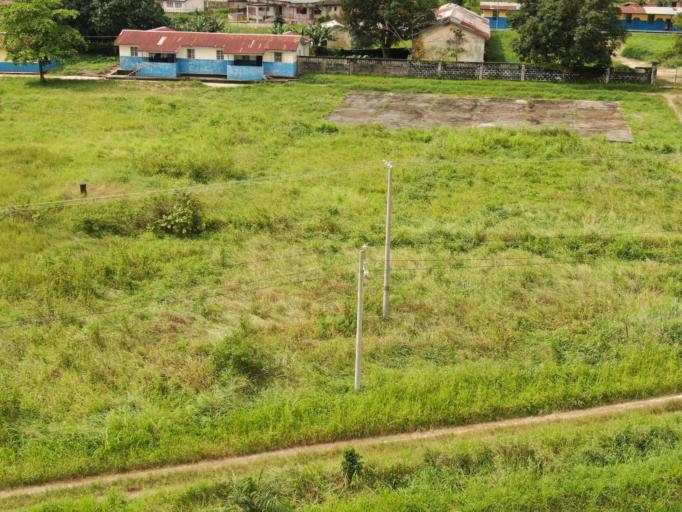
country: SL
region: Northern Province
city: Makali
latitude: 8.6300
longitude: -11.6591
